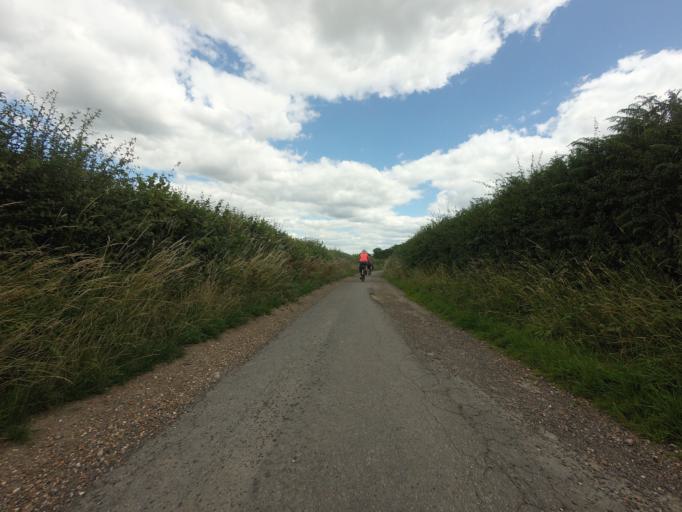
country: GB
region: England
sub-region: East Sussex
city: Hailsham
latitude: 50.8284
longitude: 0.2646
